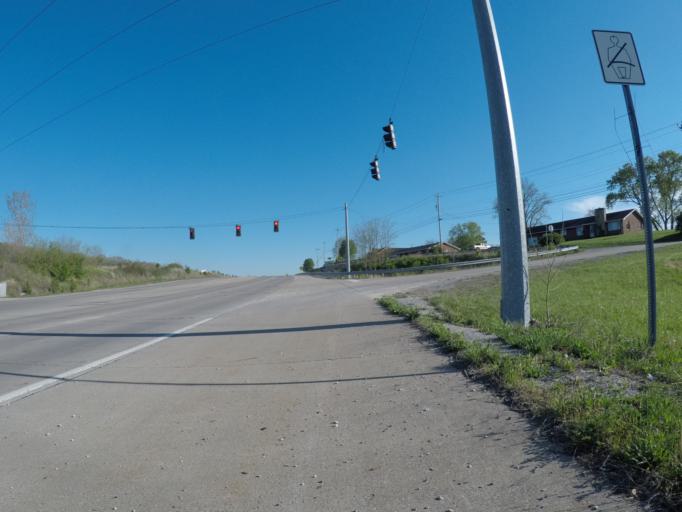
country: US
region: Kentucky
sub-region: Boyd County
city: Meads
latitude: 38.3645
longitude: -82.6990
